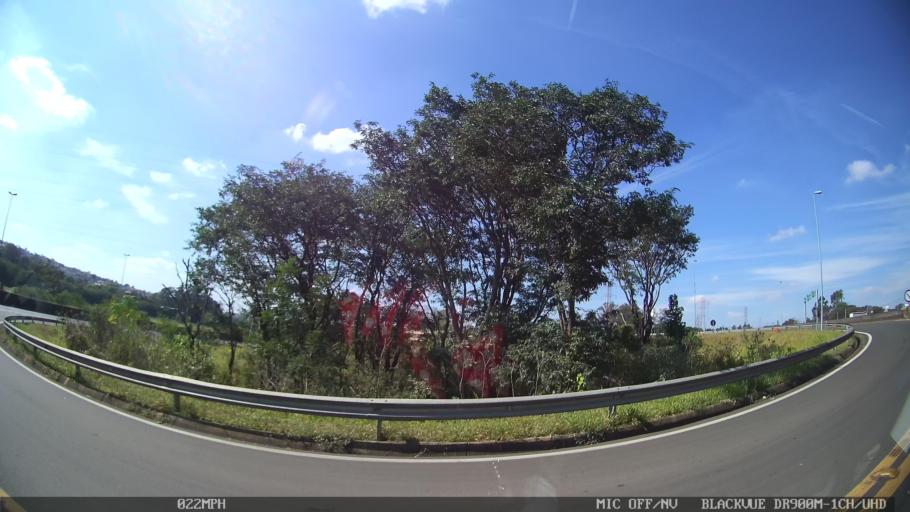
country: BR
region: Sao Paulo
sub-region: Hortolandia
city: Hortolandia
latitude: -22.8141
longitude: -47.1952
